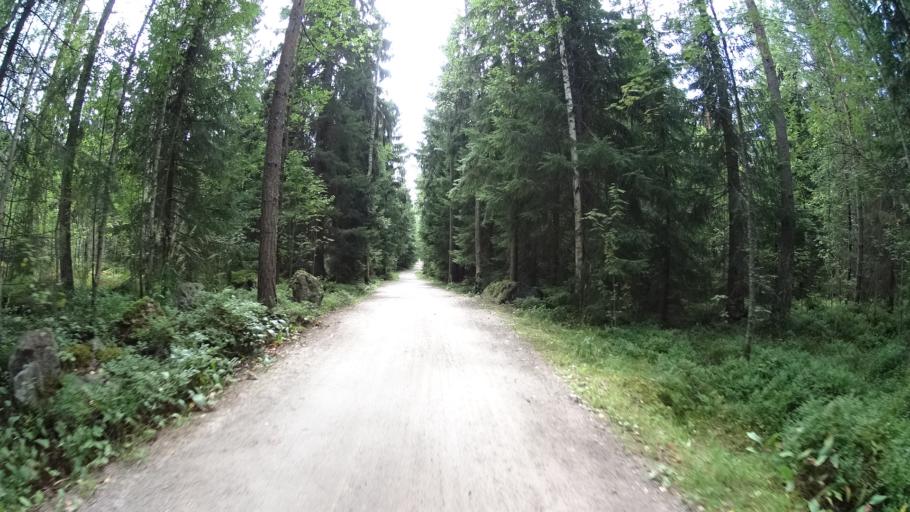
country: FI
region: Uusimaa
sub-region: Helsinki
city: Helsinki
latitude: 60.2580
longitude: 24.9050
